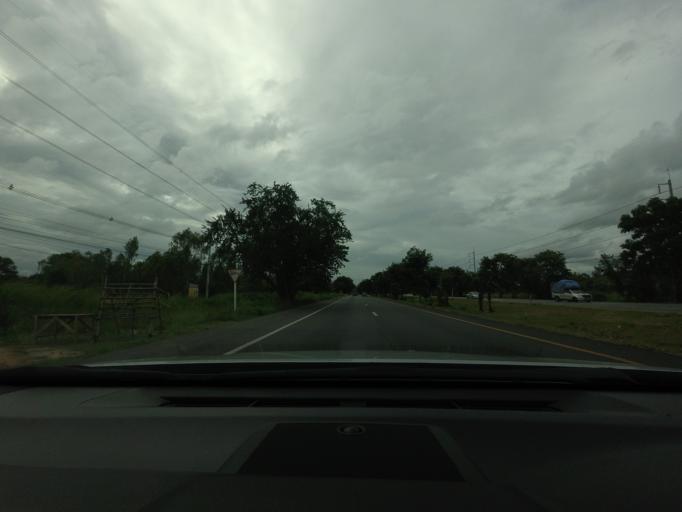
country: TH
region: Prachuap Khiri Khan
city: Hua Hin
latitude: 12.5990
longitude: 99.8627
